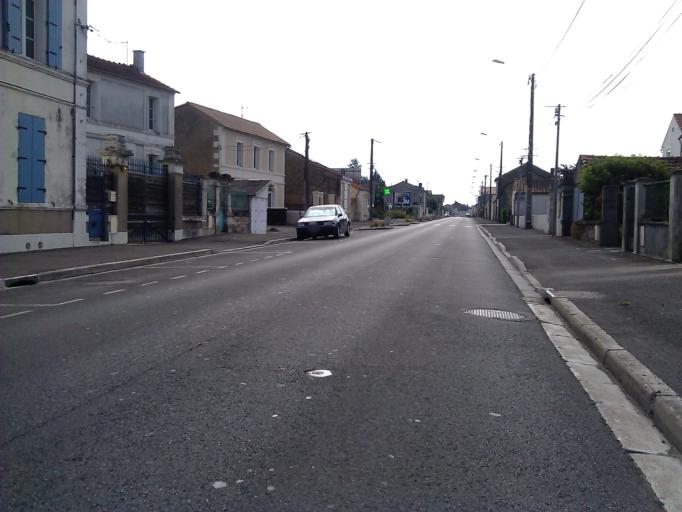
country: FR
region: Poitou-Charentes
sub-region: Departement de la Charente
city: Angouleme
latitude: 45.6624
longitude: 0.1337
